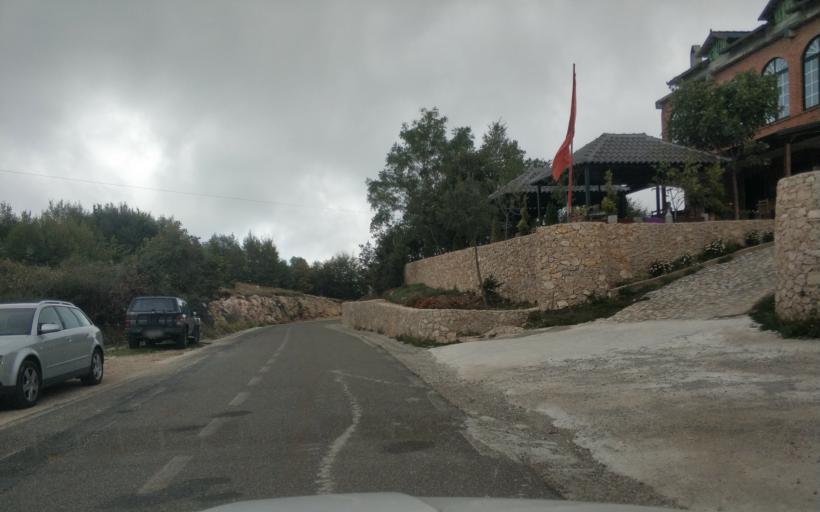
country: AL
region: Durres
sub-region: Rrethi i Krujes
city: Kruje
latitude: 41.5188
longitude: 19.8031
